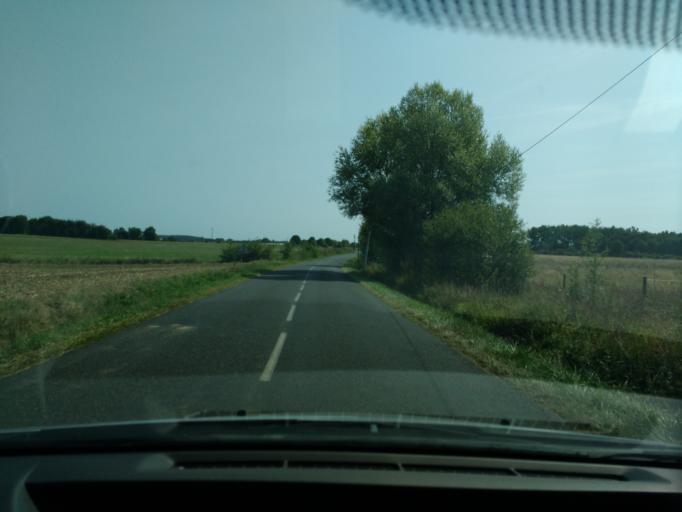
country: FR
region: Pays de la Loire
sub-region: Departement de Maine-et-Loire
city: Jarze
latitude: 47.5130
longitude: -0.1968
